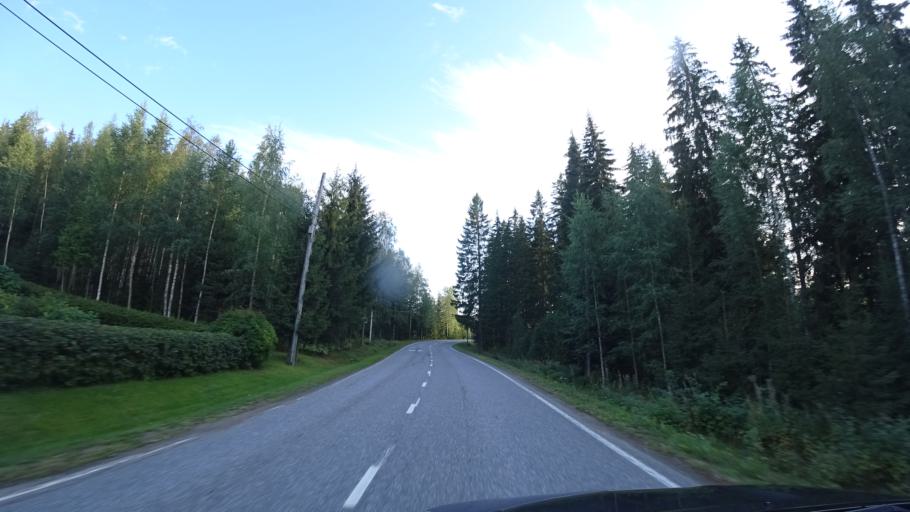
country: FI
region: Haeme
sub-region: Haemeenlinna
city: Lammi
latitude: 61.0673
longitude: 25.0023
